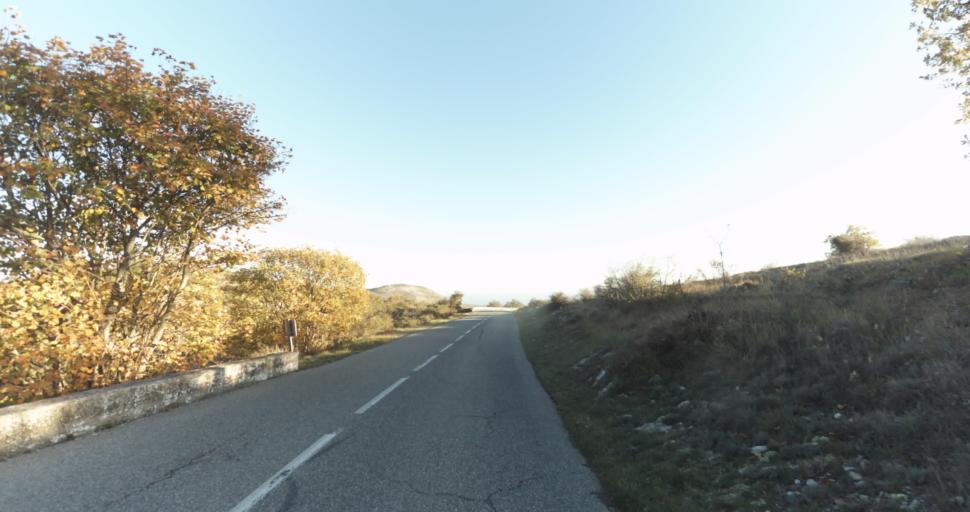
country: FR
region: Provence-Alpes-Cote d'Azur
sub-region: Departement des Alpes-Maritimes
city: Vence
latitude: 43.7596
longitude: 7.0860
